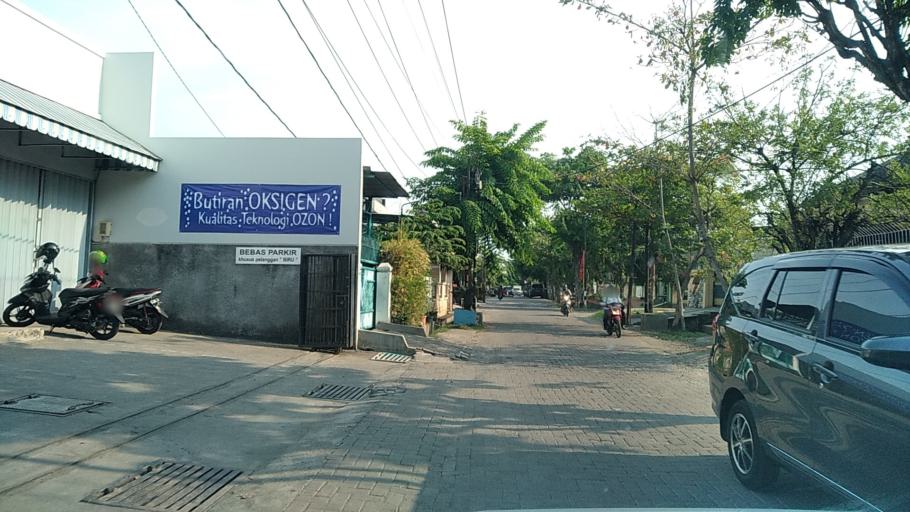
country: ID
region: Central Java
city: Semarang
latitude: -6.9570
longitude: 110.4044
